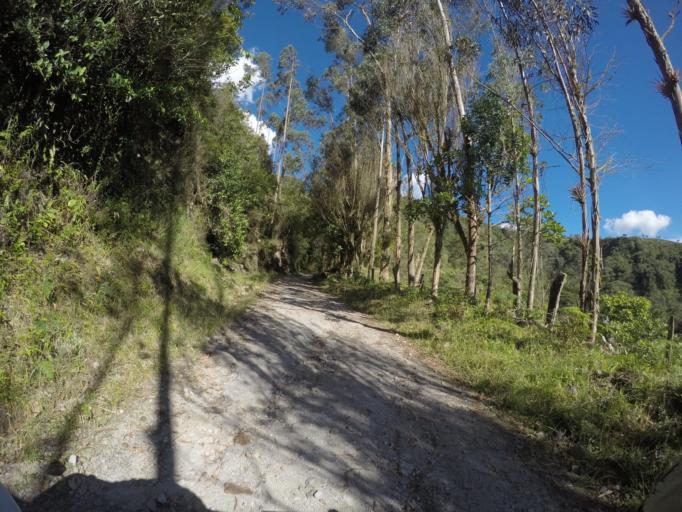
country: CO
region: Tolima
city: Cajamarca
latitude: 4.4945
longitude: -75.3976
